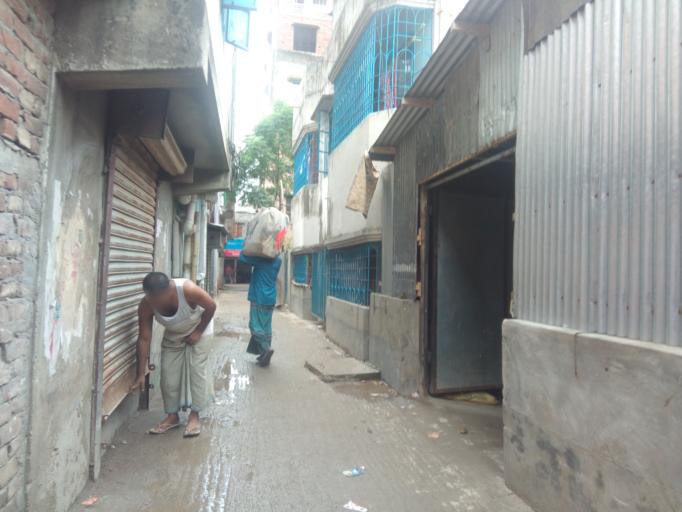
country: BD
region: Dhaka
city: Azimpur
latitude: 23.7181
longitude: 90.3737
